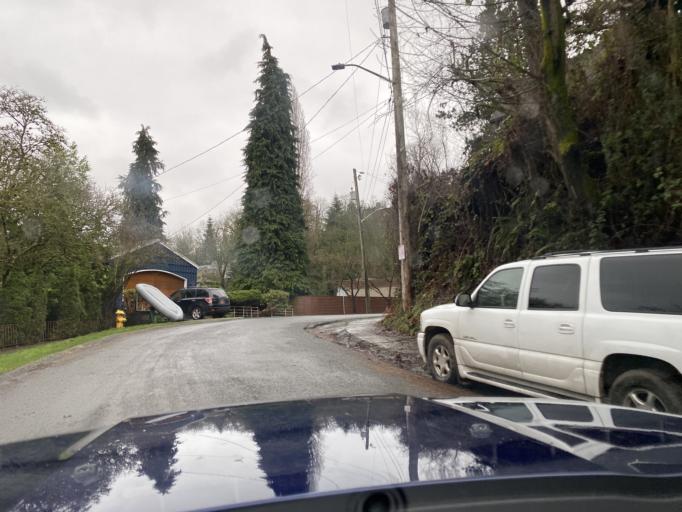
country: US
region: Washington
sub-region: King County
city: Seattle
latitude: 47.6405
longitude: -122.3133
